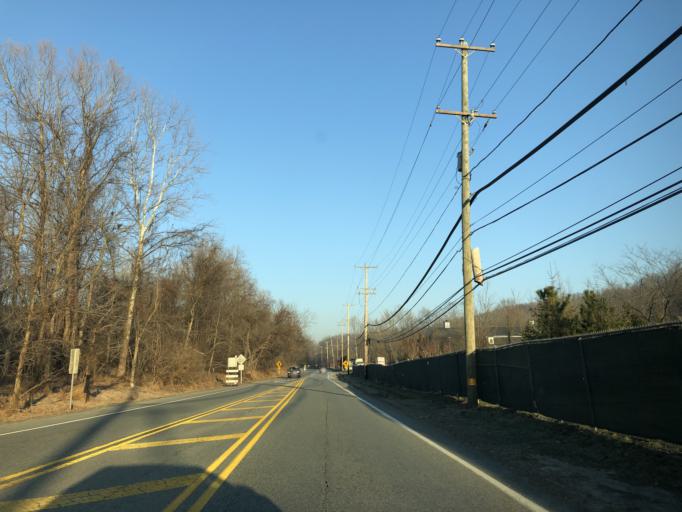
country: US
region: Pennsylvania
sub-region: Chester County
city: Downingtown
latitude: 39.9690
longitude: -75.6759
